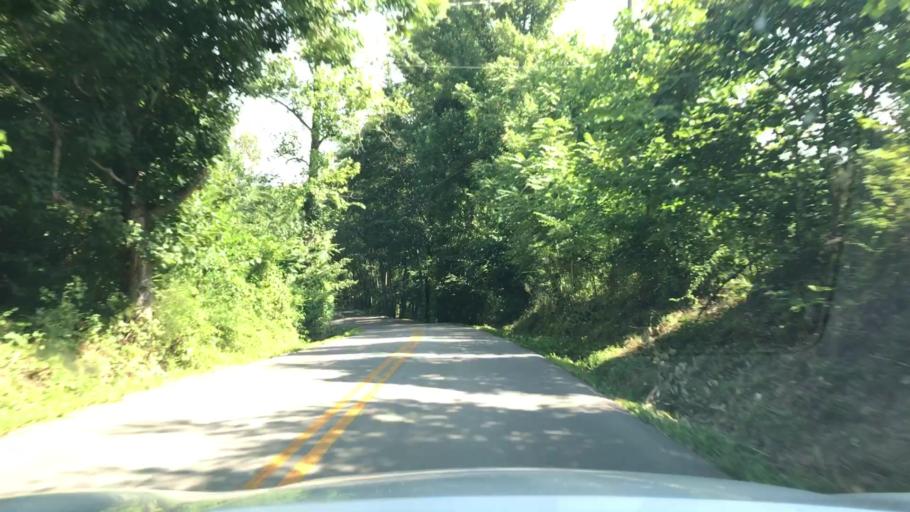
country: US
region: Kentucky
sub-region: Clinton County
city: Albany
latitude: 36.6466
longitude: -85.0795
